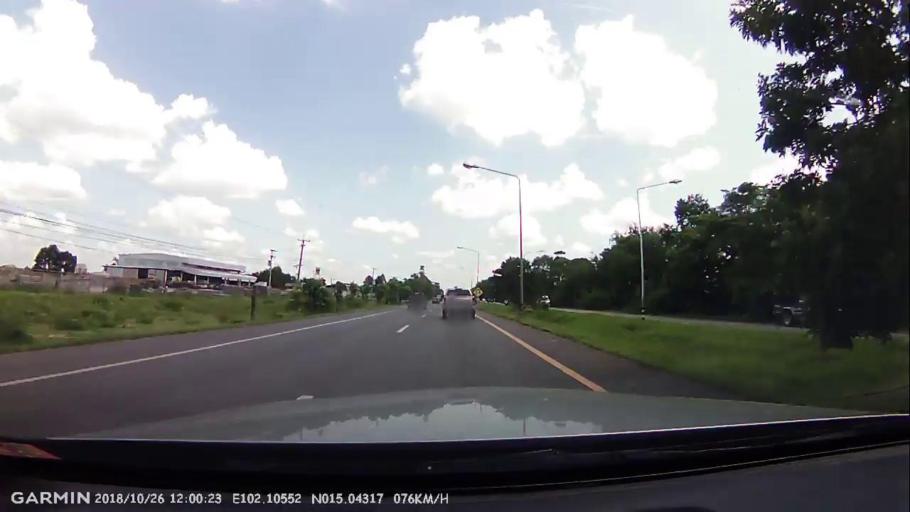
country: TH
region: Nakhon Ratchasima
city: Nakhon Ratchasima
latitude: 15.0432
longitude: 102.1057
